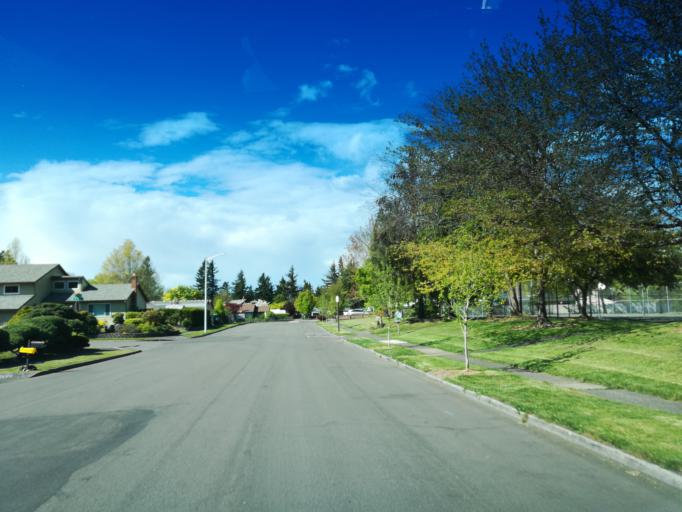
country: US
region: Oregon
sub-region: Multnomah County
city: Troutdale
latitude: 45.5269
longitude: -122.3827
